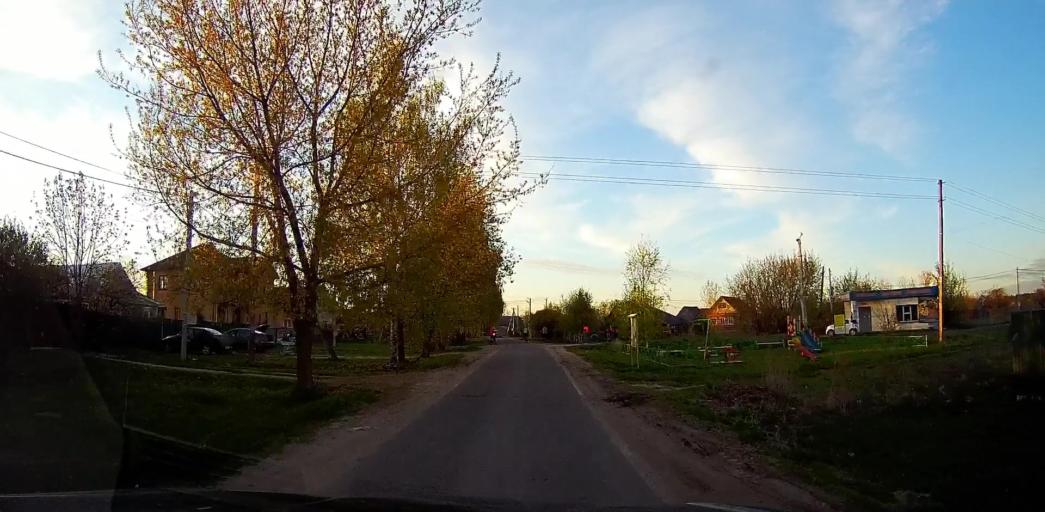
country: RU
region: Moskovskaya
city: Peski
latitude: 55.2084
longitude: 38.7392
